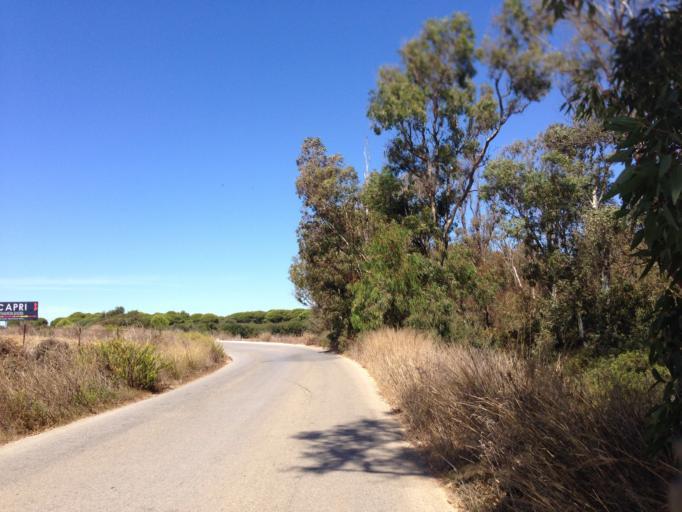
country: ES
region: Andalusia
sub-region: Provincia de Cadiz
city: Chiclana de la Frontera
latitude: 36.3324
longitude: -6.1561
